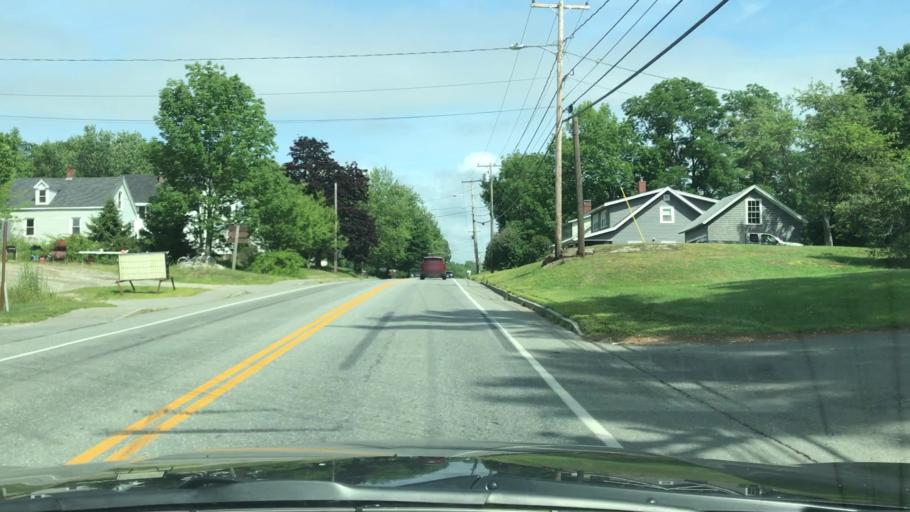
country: US
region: Maine
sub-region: Hancock County
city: Bucksport
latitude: 44.5708
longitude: -68.7830
